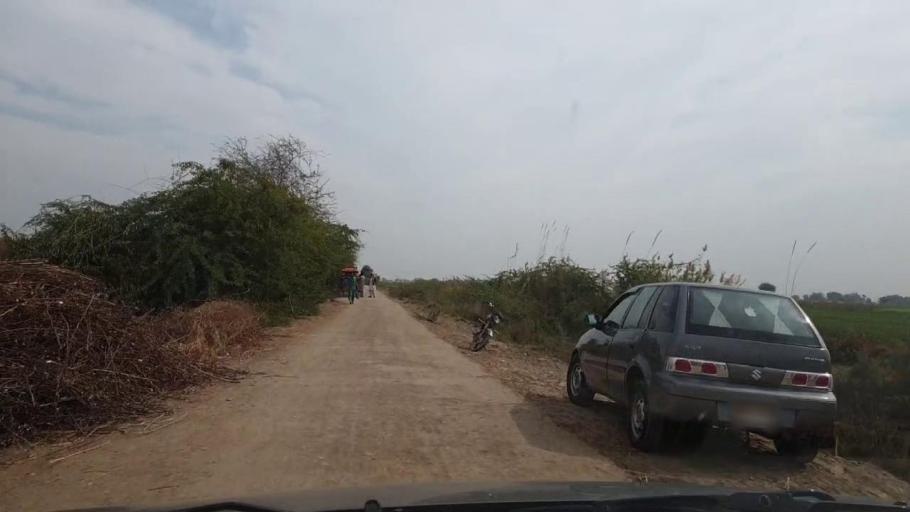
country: PK
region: Sindh
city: Sinjhoro
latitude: 26.0648
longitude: 68.8419
